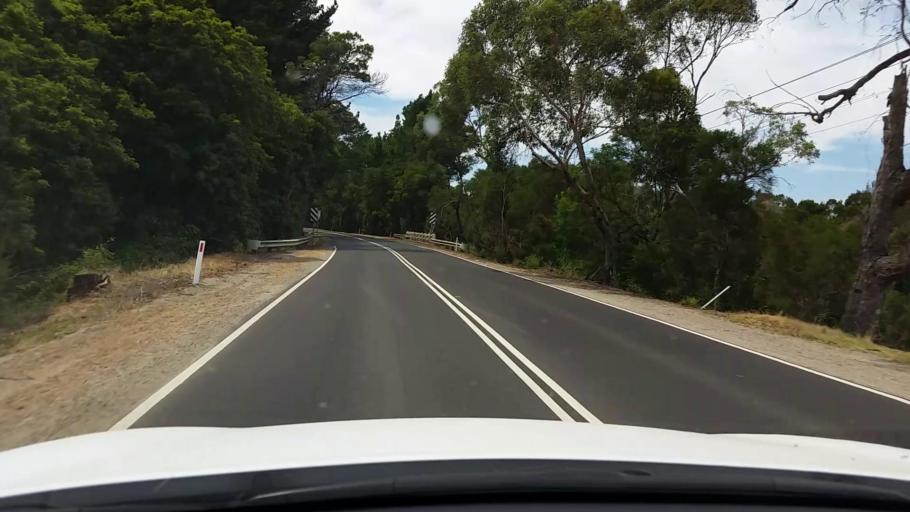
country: AU
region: Victoria
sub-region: Mornington Peninsula
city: Mount Martha
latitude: -38.2803
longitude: 145.0703
